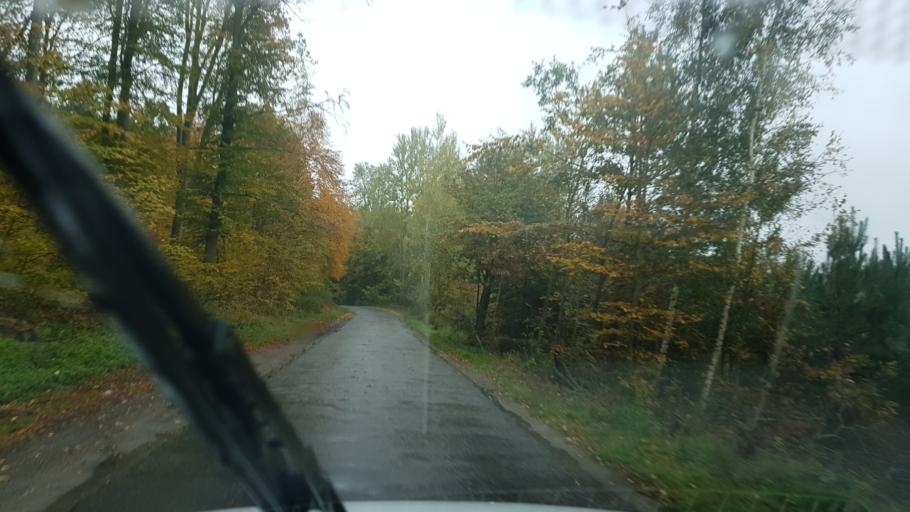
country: PL
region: West Pomeranian Voivodeship
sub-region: Powiat mysliborski
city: Barlinek
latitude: 53.0168
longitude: 15.2218
